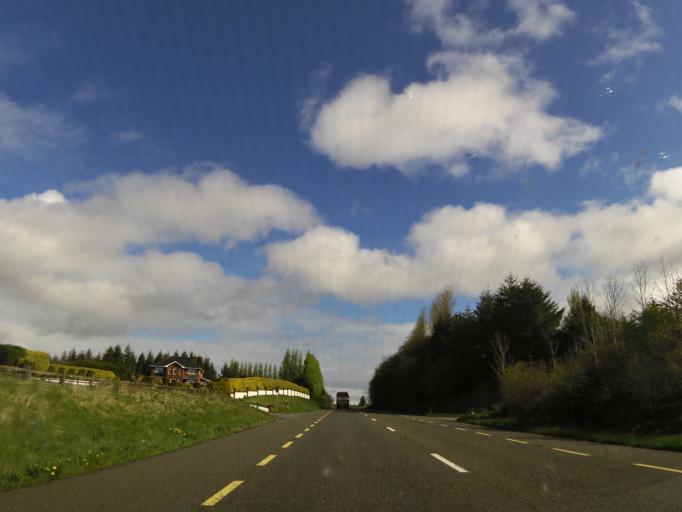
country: IE
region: Connaught
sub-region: Maigh Eo
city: Ballyhaunis
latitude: 53.8900
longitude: -8.8012
